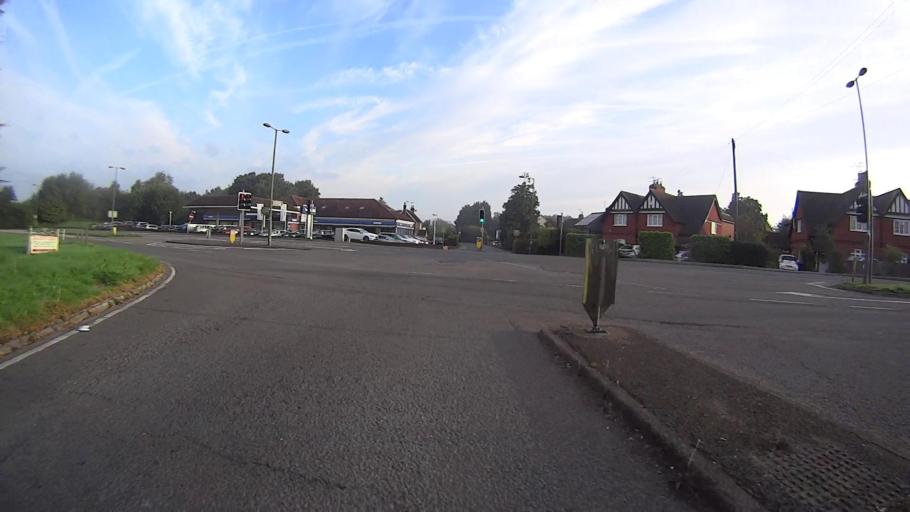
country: GB
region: England
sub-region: West Sussex
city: Copthorne
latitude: 51.1531
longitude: -0.1110
